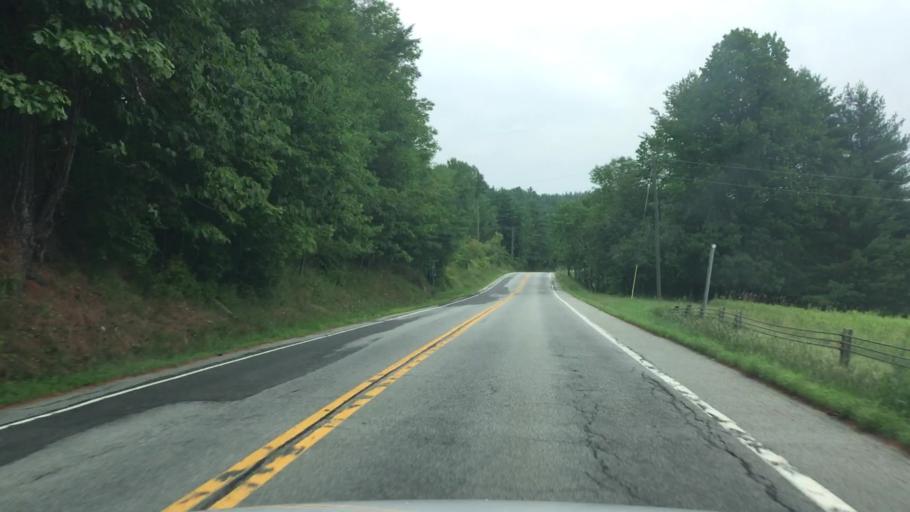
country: US
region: New York
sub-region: Essex County
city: Elizabethtown
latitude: 44.3993
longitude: -73.7075
